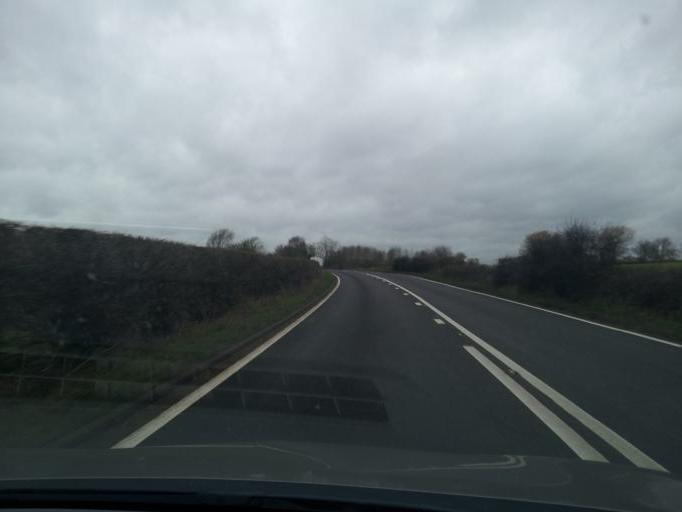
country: GB
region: England
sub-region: Suffolk
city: Botesdale
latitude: 52.3284
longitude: 0.9372
